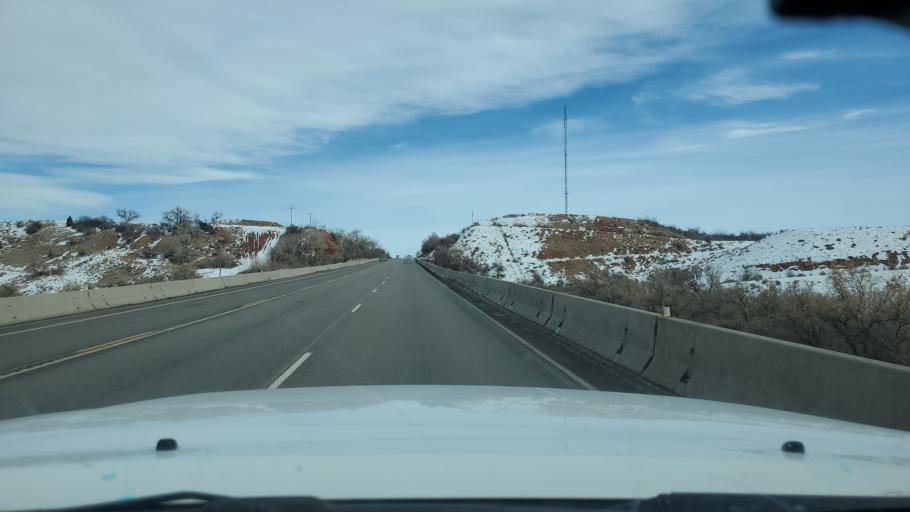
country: US
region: Utah
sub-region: Duchesne County
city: Roosevelt
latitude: 40.3019
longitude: -109.9083
